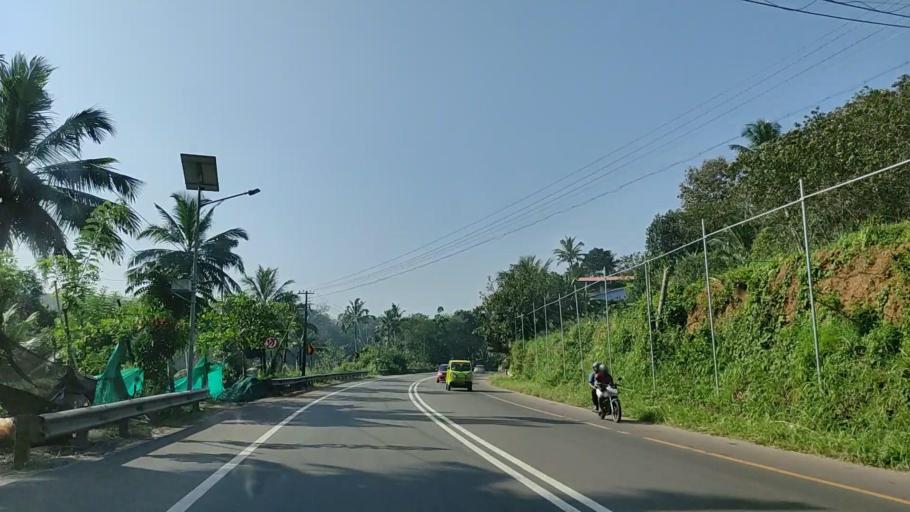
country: IN
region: Kerala
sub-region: Kollam
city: Punalur
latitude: 8.8833
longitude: 76.8693
